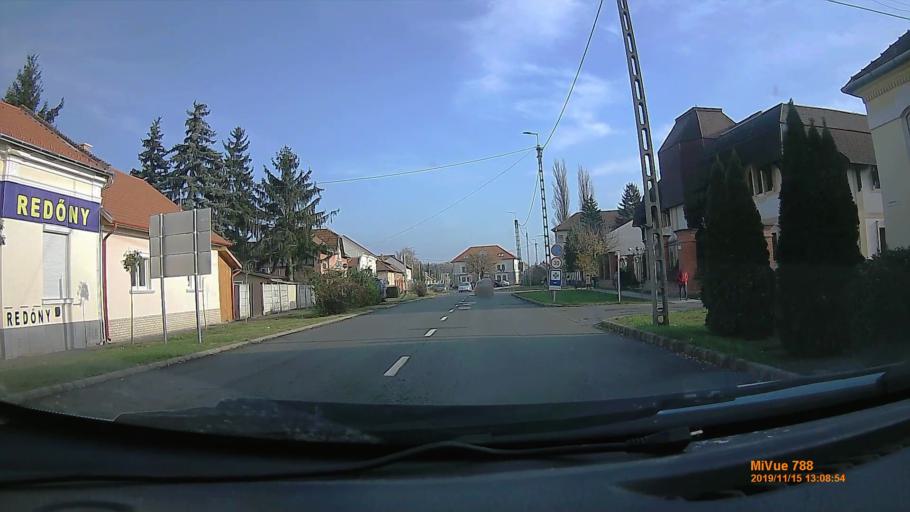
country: HU
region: Bekes
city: Gyula
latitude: 46.6431
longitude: 21.2745
